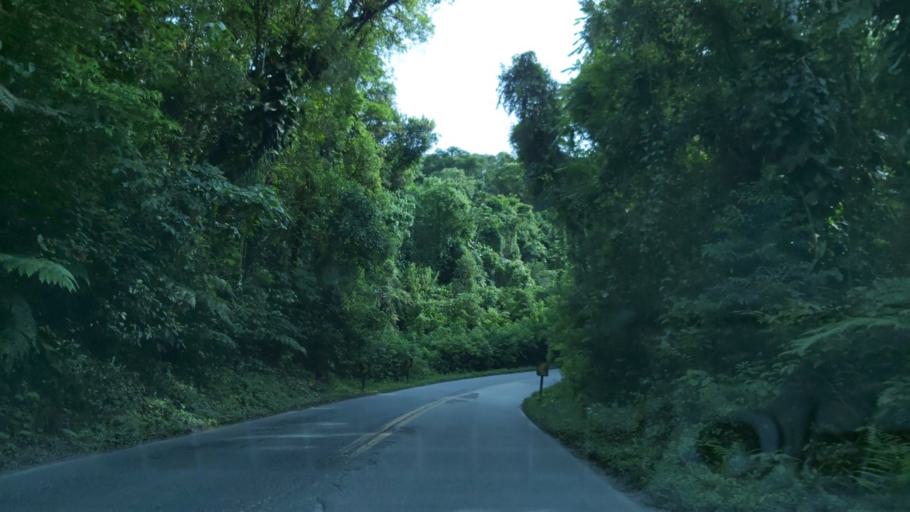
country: BR
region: Sao Paulo
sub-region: Juquia
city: Juquia
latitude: -24.0997
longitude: -47.6243
